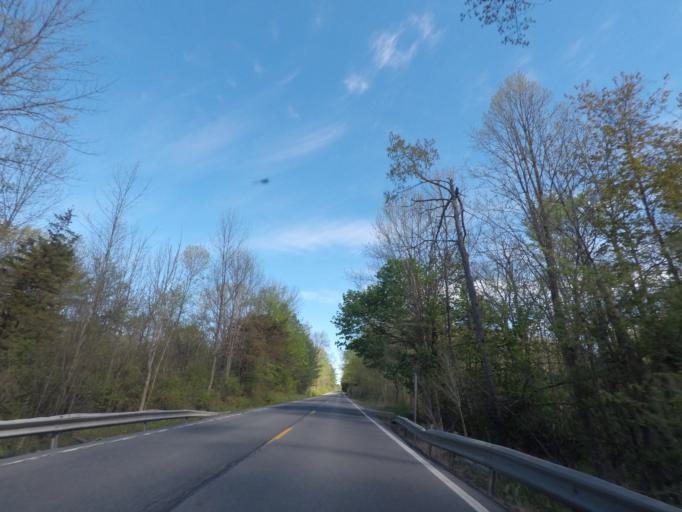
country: US
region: New York
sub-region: Albany County
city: Ravena
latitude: 42.4933
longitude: -73.9412
